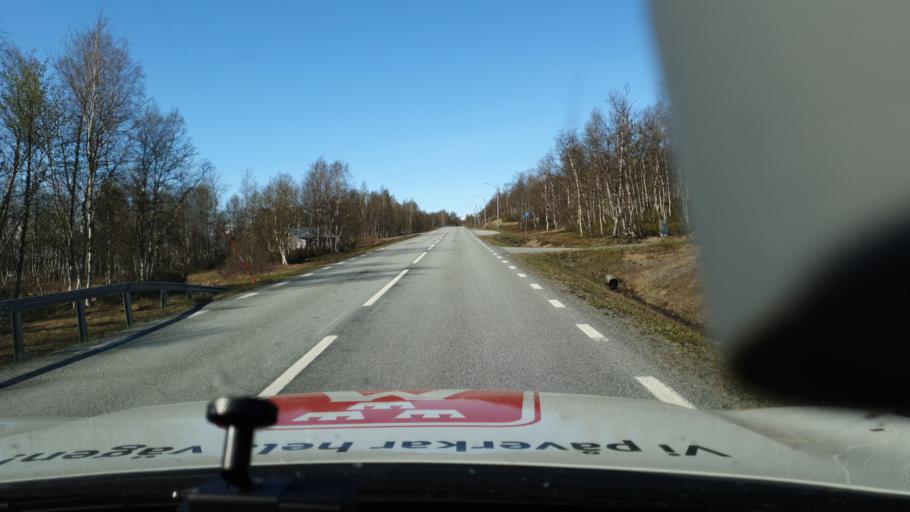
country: NO
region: Nordland
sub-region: Rana
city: Mo i Rana
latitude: 65.9779
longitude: 15.0643
